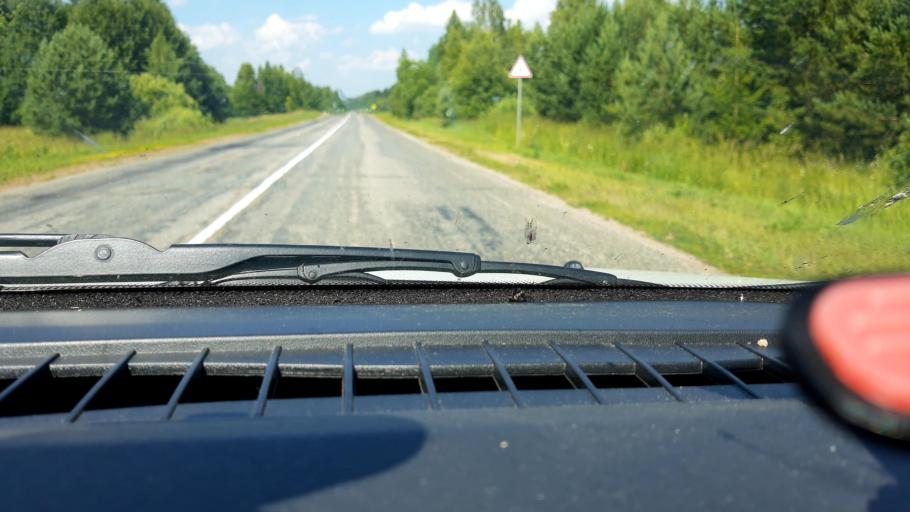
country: RU
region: Nizjnij Novgorod
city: Tonkino
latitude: 57.3167
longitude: 46.4706
